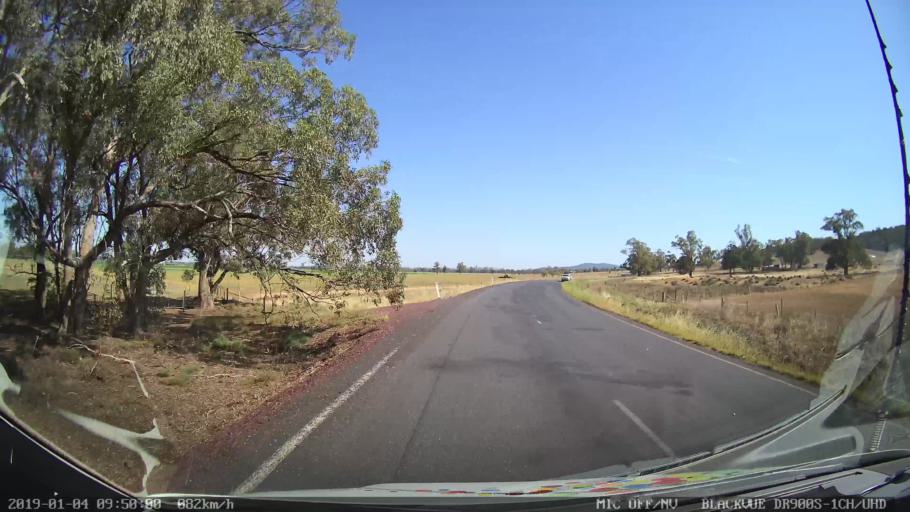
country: AU
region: New South Wales
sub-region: Cabonne
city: Canowindra
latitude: -33.5893
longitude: 148.4150
